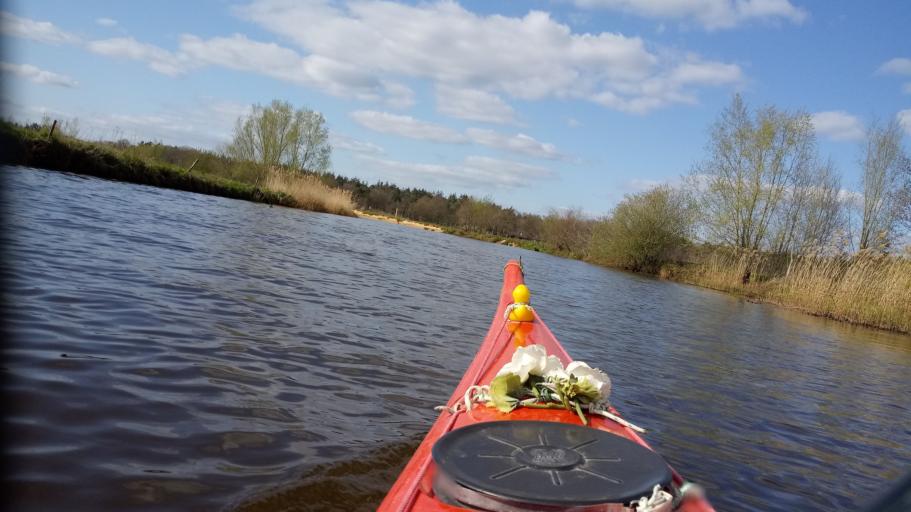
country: NL
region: Overijssel
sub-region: Gemeente Twenterand
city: Den Ham
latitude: 52.4996
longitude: 6.4118
